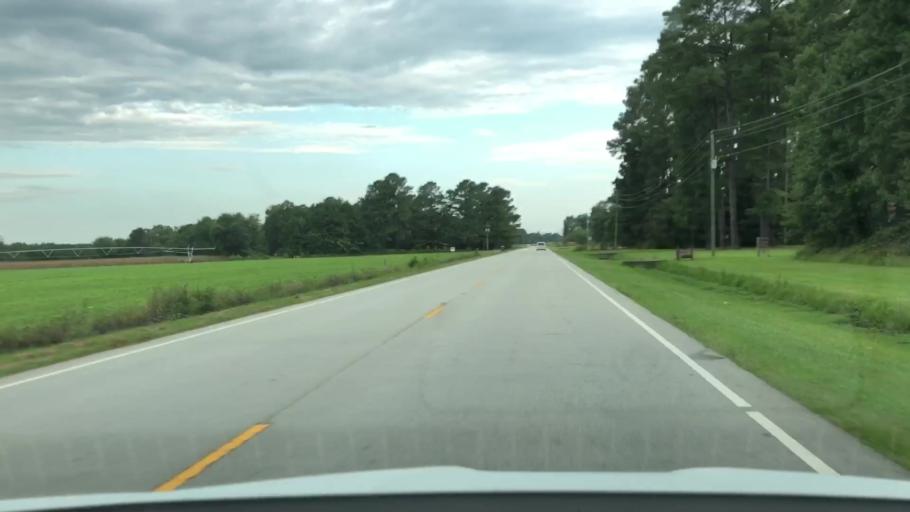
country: US
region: North Carolina
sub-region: Jones County
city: Trenton
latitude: 35.0757
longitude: -77.3905
